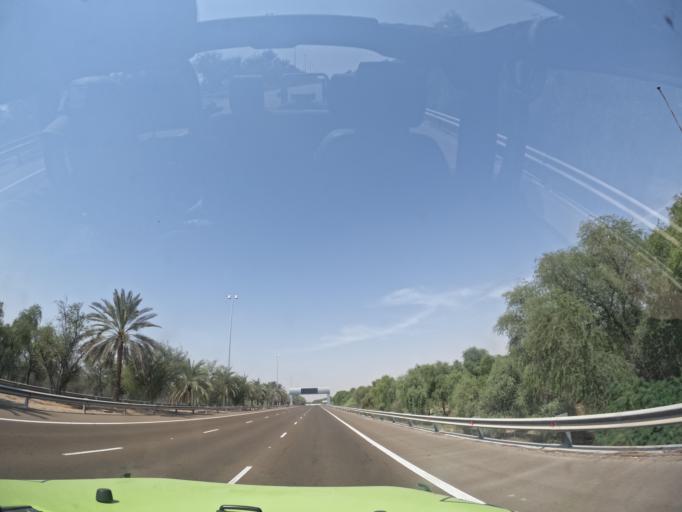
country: AE
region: Abu Dhabi
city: Al Ain
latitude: 24.1795
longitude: 55.1678
